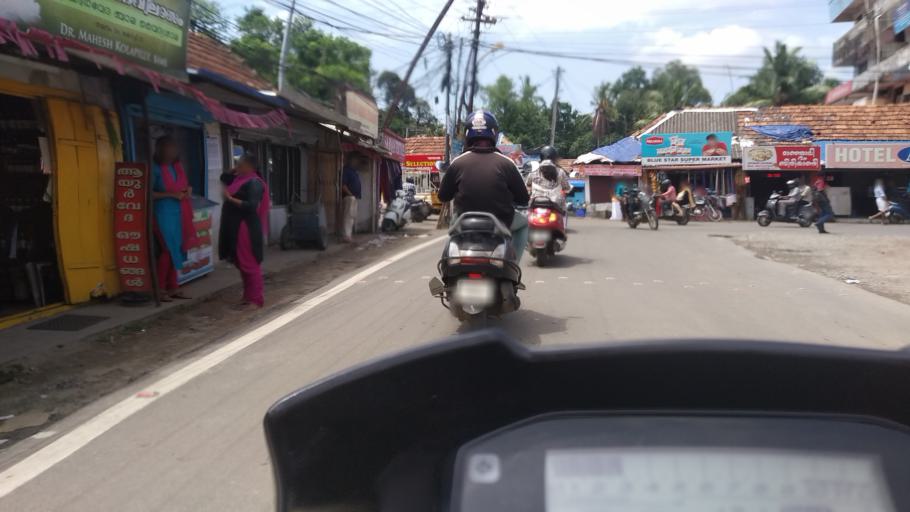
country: IN
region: Kerala
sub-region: Ernakulam
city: Cochin
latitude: 9.9864
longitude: 76.3107
